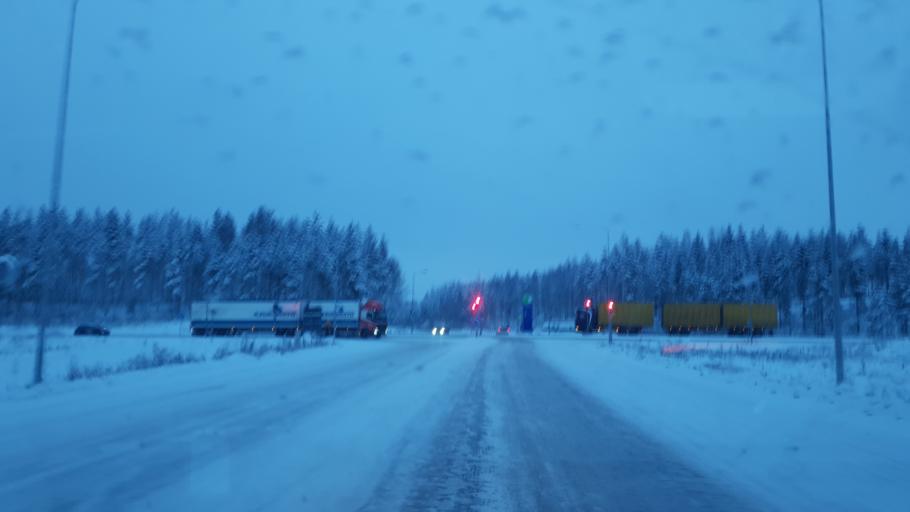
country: FI
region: Uusimaa
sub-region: Helsinki
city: Kerava
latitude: 60.3826
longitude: 25.1669
